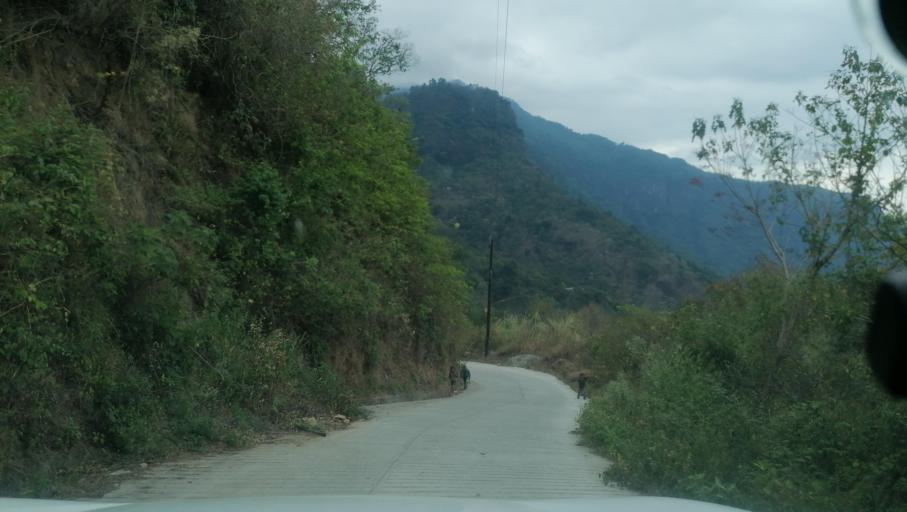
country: MX
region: Chiapas
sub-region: Cacahoatan
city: Benito Juarez
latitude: 15.1637
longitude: -92.1750
